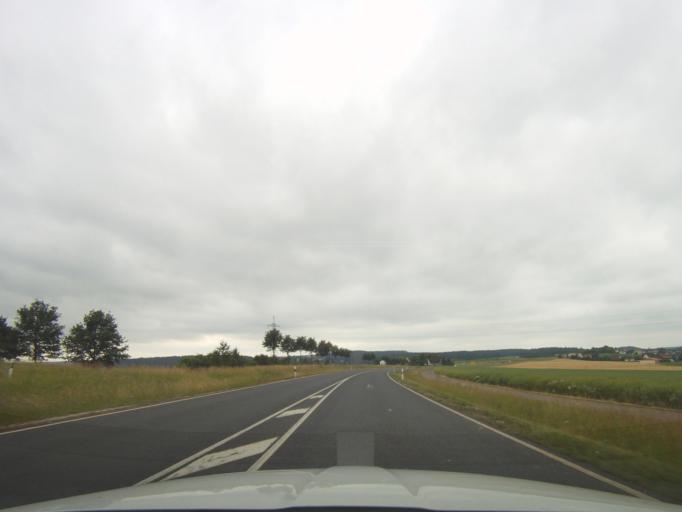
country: DE
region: Bavaria
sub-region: Upper Franconia
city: Ahorn
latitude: 50.2332
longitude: 10.9299
